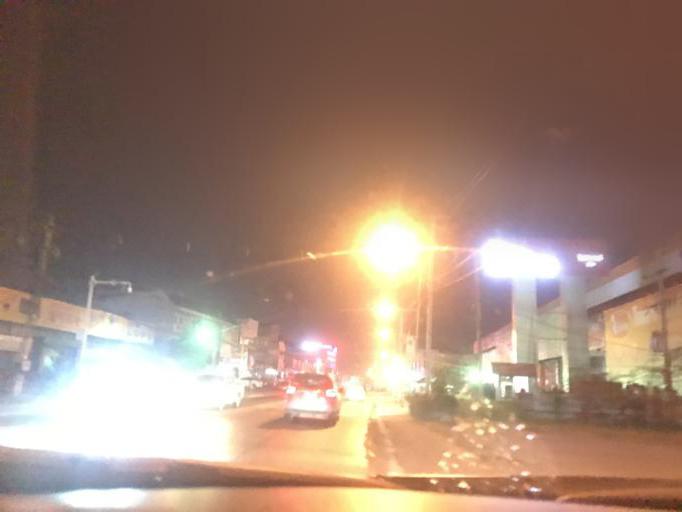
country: LA
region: Vientiane
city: Vientiane
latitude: 17.9763
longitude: 102.5844
